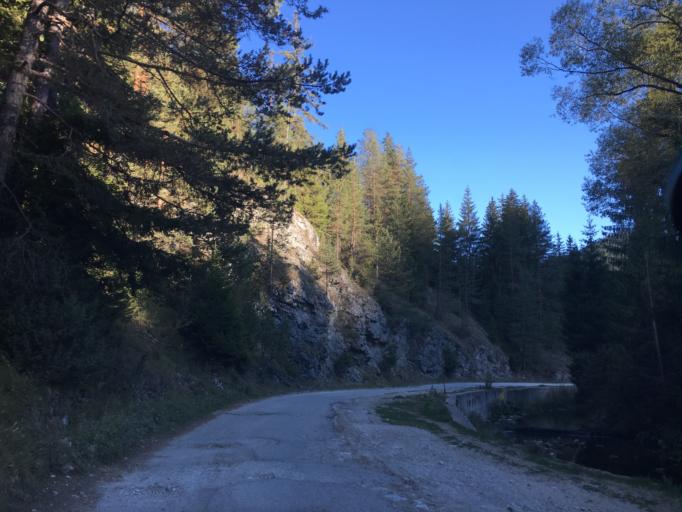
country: BG
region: Smolyan
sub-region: Obshtina Borino
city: Borino
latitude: 41.5880
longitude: 24.3864
